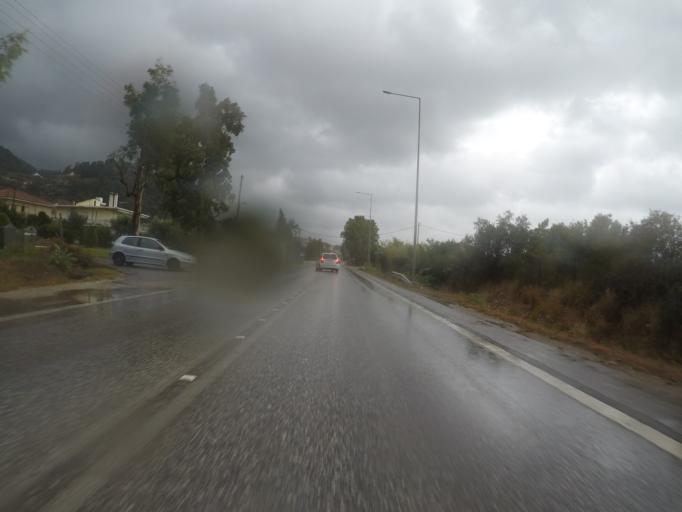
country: GR
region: Peloponnese
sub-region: Nomos Messinias
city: Kyparissia
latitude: 37.2560
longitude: 21.6799
